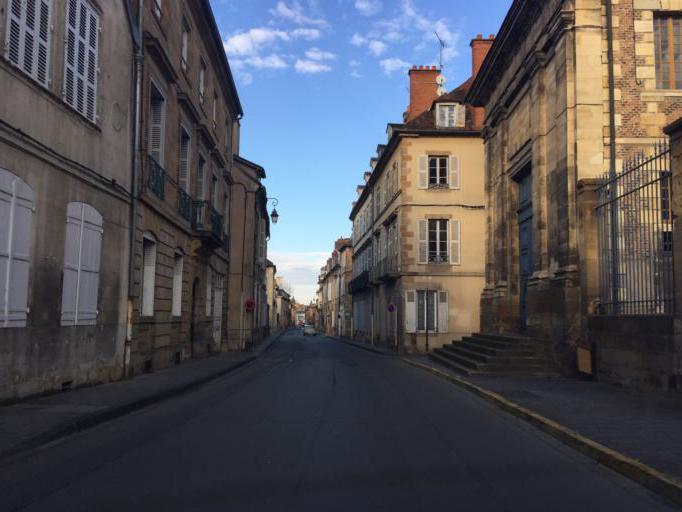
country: FR
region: Auvergne
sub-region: Departement de l'Allier
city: Moulins
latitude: 46.5685
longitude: 3.3304
